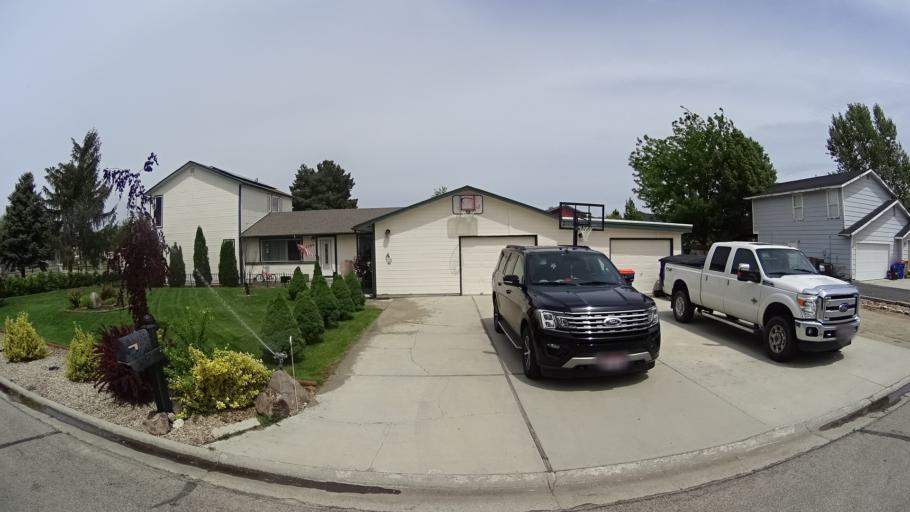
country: US
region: Idaho
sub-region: Ada County
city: Meridian
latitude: 43.5566
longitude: -116.3290
